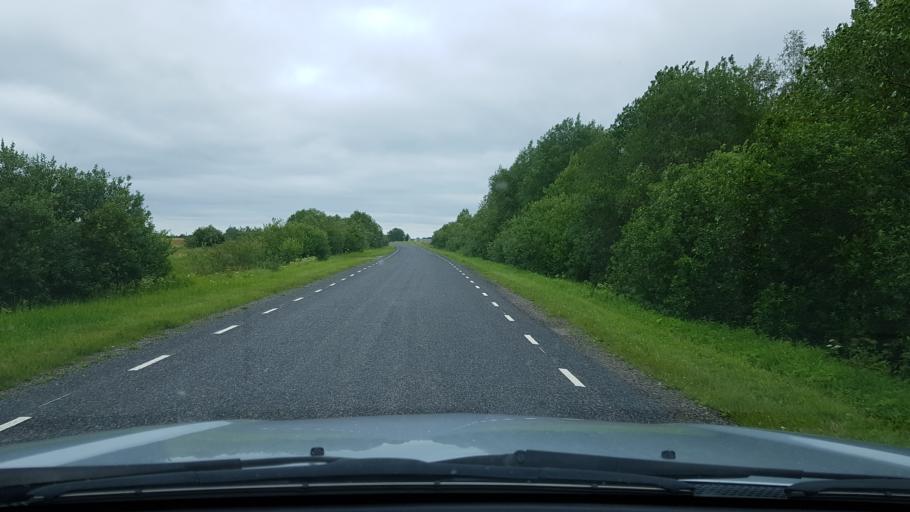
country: EE
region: Ida-Virumaa
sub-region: Narva linn
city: Narva
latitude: 59.3758
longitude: 28.1157
